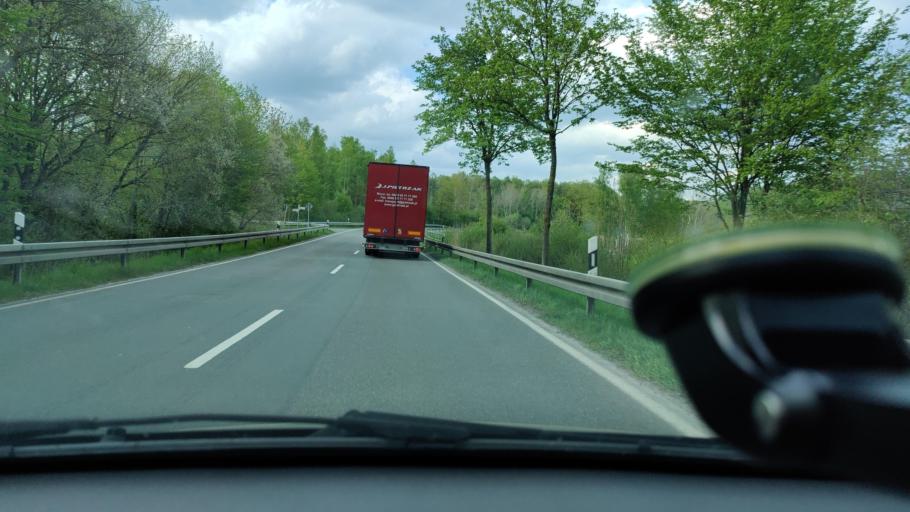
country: DE
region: North Rhine-Westphalia
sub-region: Regierungsbezirk Detmold
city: Wunnenberg
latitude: 51.4813
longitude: 8.6561
